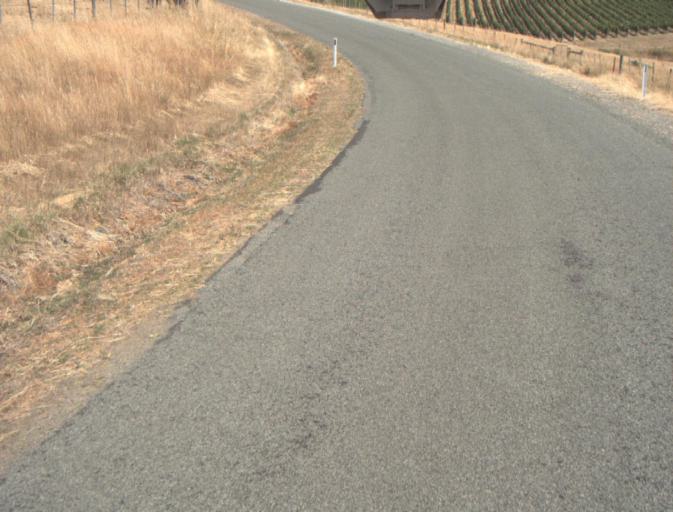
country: AU
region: Tasmania
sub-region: Launceston
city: Newstead
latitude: -41.4962
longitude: 147.2137
